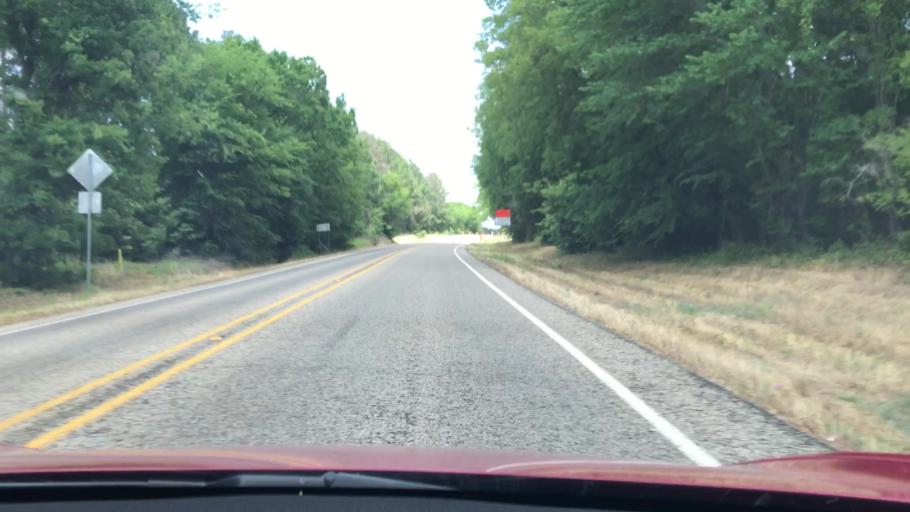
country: US
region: Texas
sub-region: Smith County
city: Hideaway
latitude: 32.4823
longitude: -95.4440
